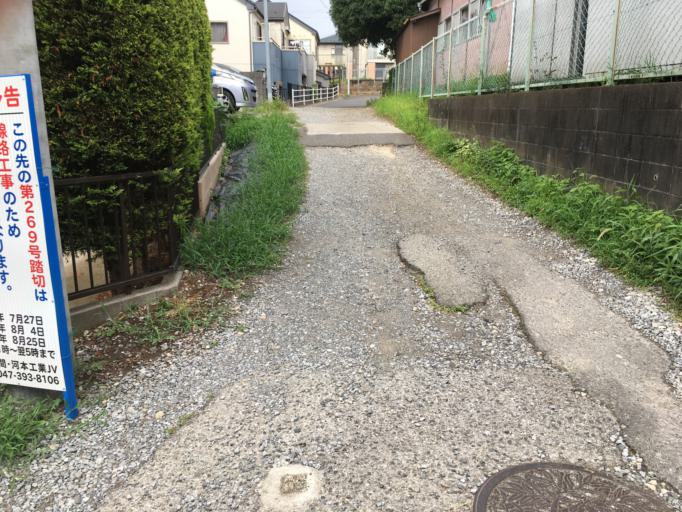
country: JP
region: Chiba
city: Kashiwa
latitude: 35.7956
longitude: 139.9986
